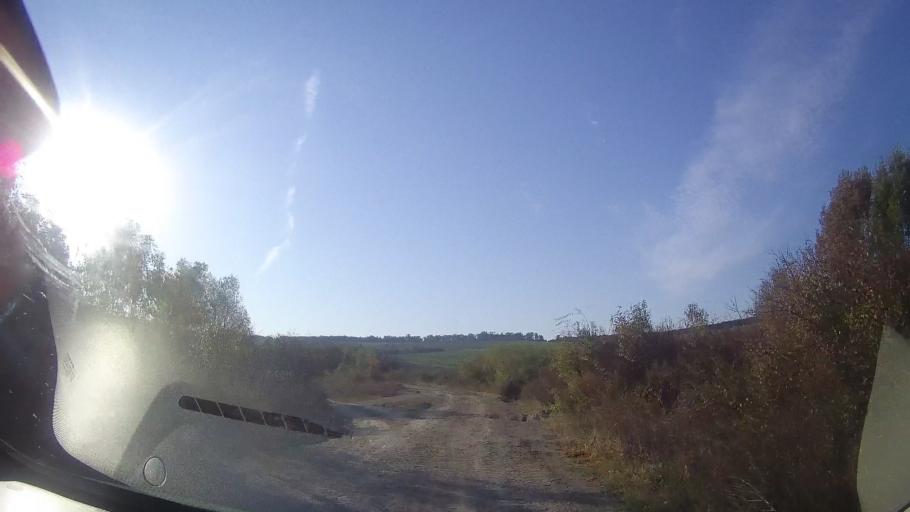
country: RO
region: Timis
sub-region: Comuna Bogda
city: Bogda
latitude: 45.9535
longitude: 21.6145
